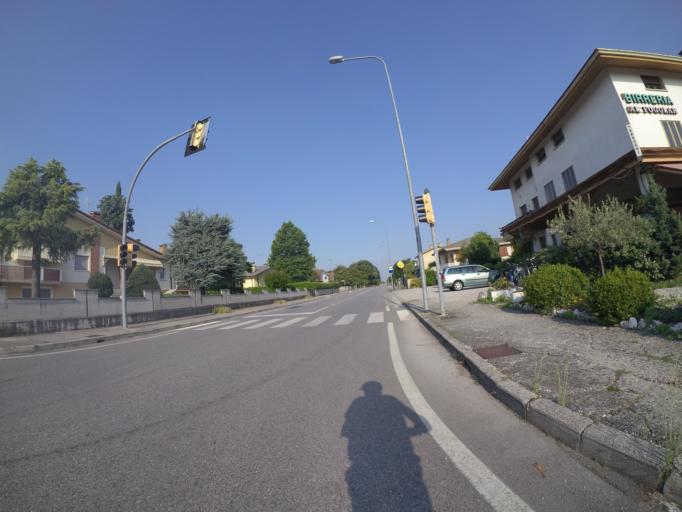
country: IT
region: Friuli Venezia Giulia
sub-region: Provincia di Udine
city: Codroipo
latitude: 45.9591
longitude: 12.9920
